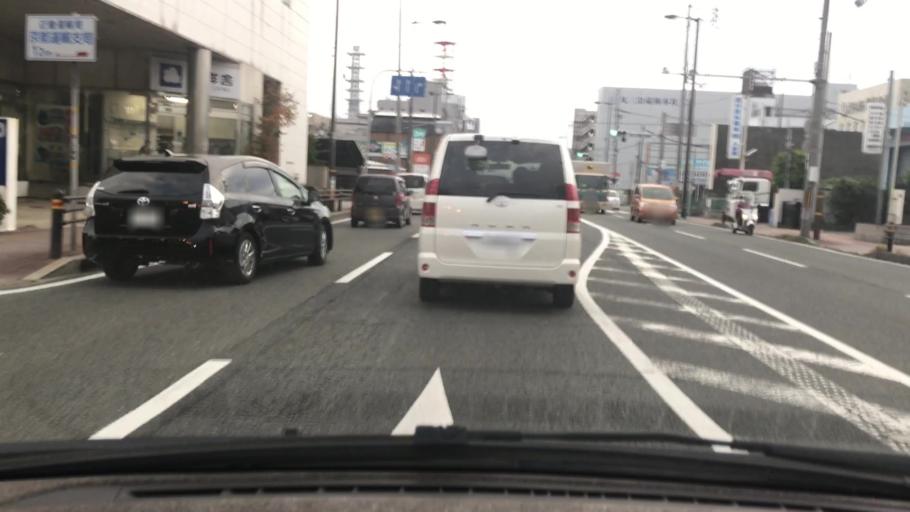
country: JP
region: Kyoto
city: Muko
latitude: 34.9664
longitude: 135.7459
